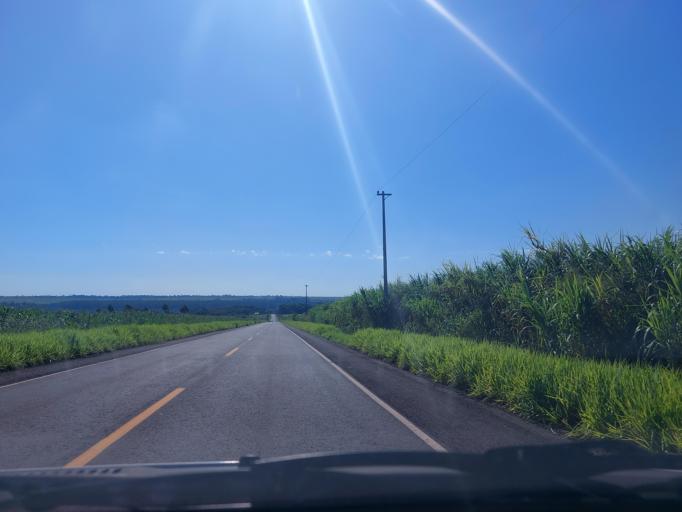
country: PY
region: San Pedro
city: Guayaybi
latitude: -24.3083
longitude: -56.1510
